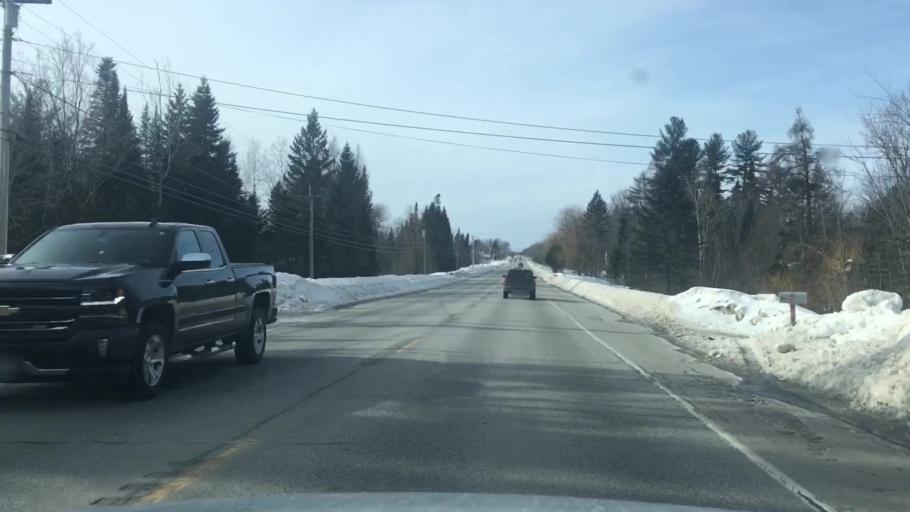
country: US
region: Maine
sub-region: Penobscot County
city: Kenduskeag
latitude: 44.9774
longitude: -68.9901
